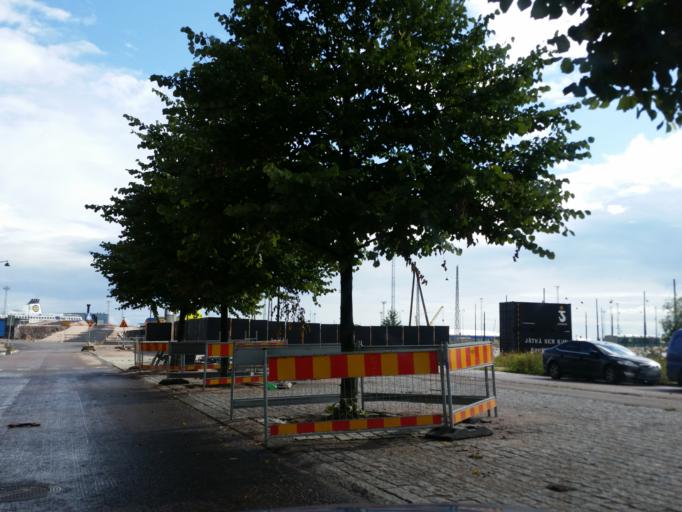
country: FI
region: Uusimaa
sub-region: Helsinki
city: Helsinki
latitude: 60.1591
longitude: 24.9116
